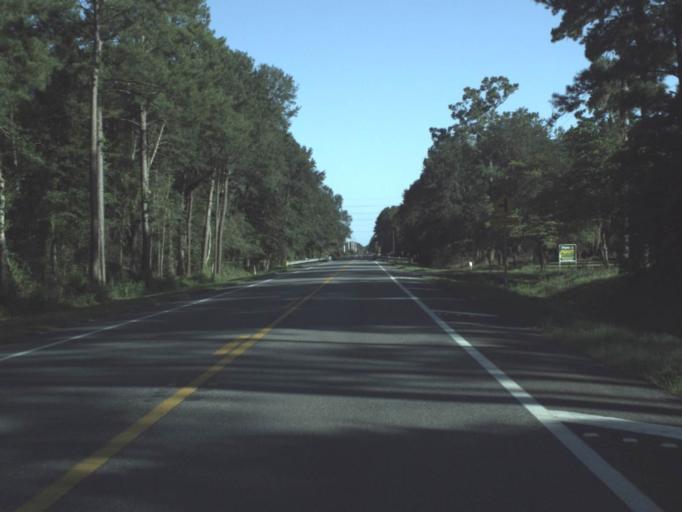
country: US
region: Florida
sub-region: Taylor County
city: Perry
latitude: 30.1626
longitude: -83.5945
